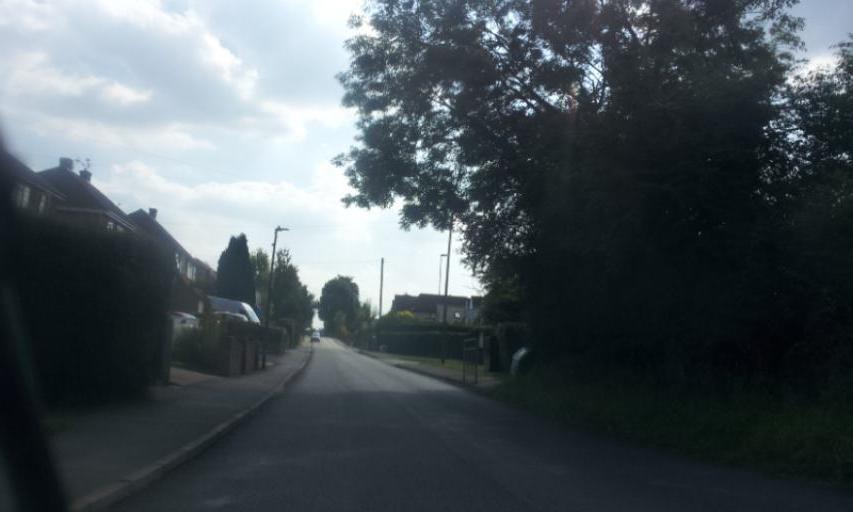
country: GB
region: England
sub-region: Kent
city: Maidstone
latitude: 51.2365
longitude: 0.4966
